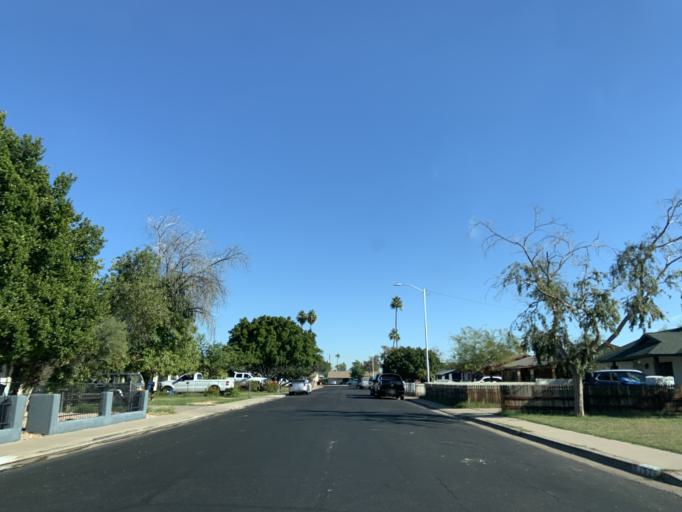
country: US
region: Arizona
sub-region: Maricopa County
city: Mesa
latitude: 33.4051
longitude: -111.8645
